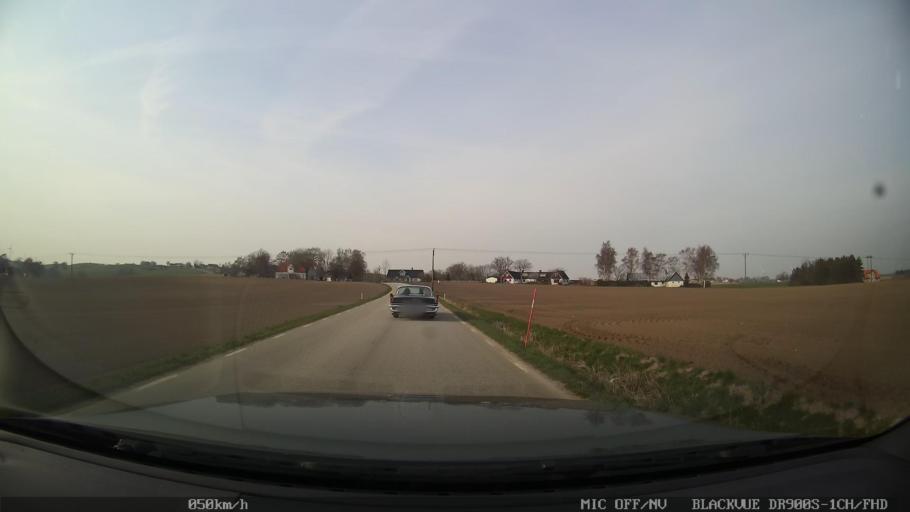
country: SE
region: Skane
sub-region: Ystads Kommun
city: Ystad
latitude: 55.4618
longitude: 13.8247
